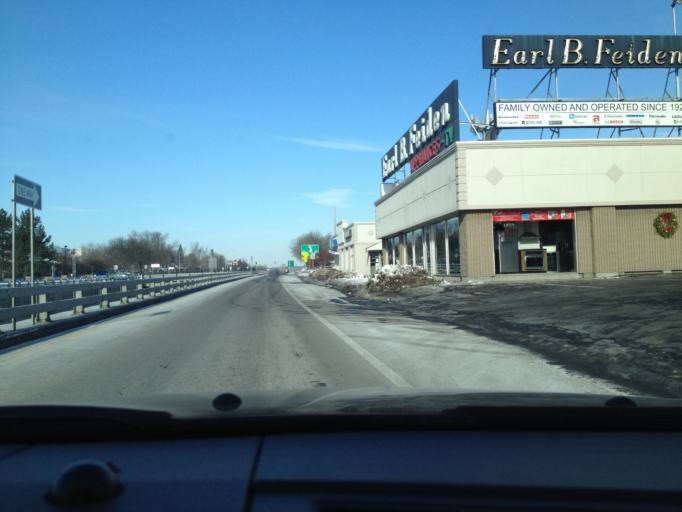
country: US
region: New York
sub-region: Albany County
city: Watervliet
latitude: 42.7458
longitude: -73.7615
